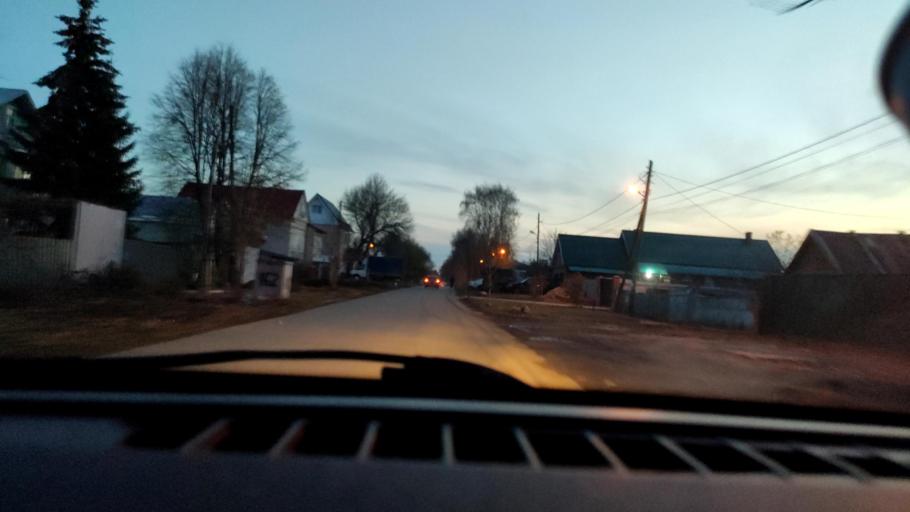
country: RU
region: Samara
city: Petra-Dubrava
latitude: 53.2598
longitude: 50.3298
